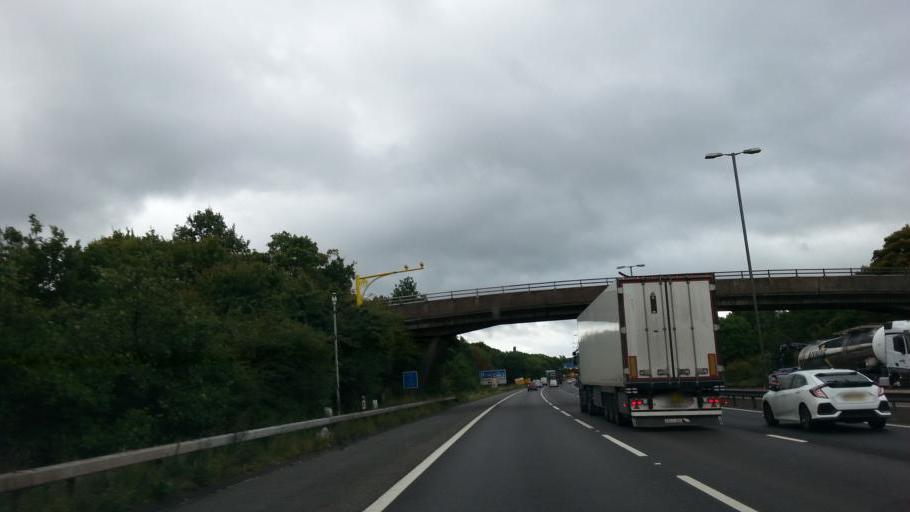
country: GB
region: England
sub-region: Sandwell
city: West Bromwich
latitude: 52.5250
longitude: -1.9701
